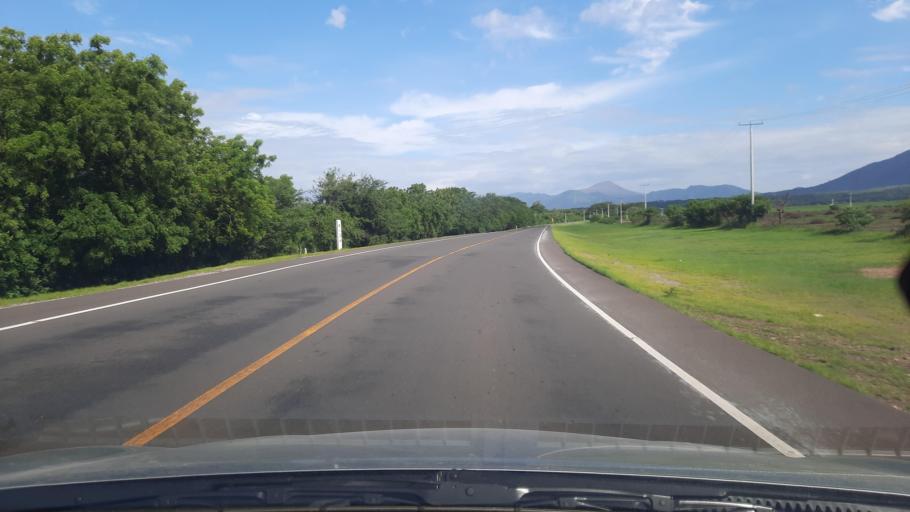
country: NI
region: Chinandega
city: Chichigalpa
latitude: 12.7623
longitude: -86.8999
